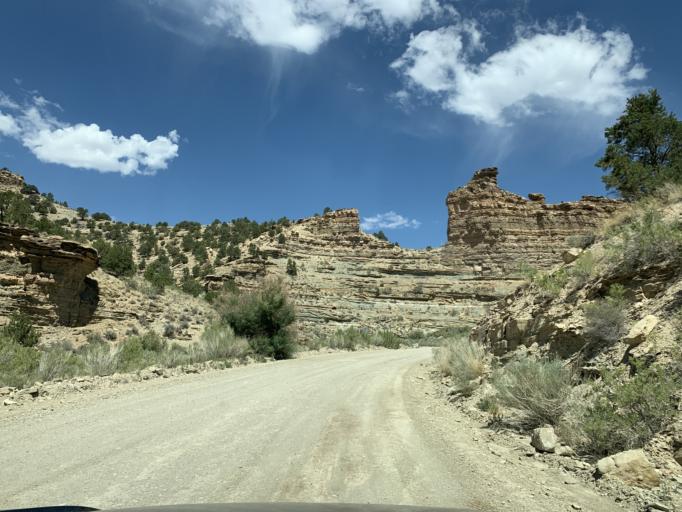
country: US
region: Utah
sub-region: Carbon County
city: East Carbon City
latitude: 39.8282
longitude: -110.2486
